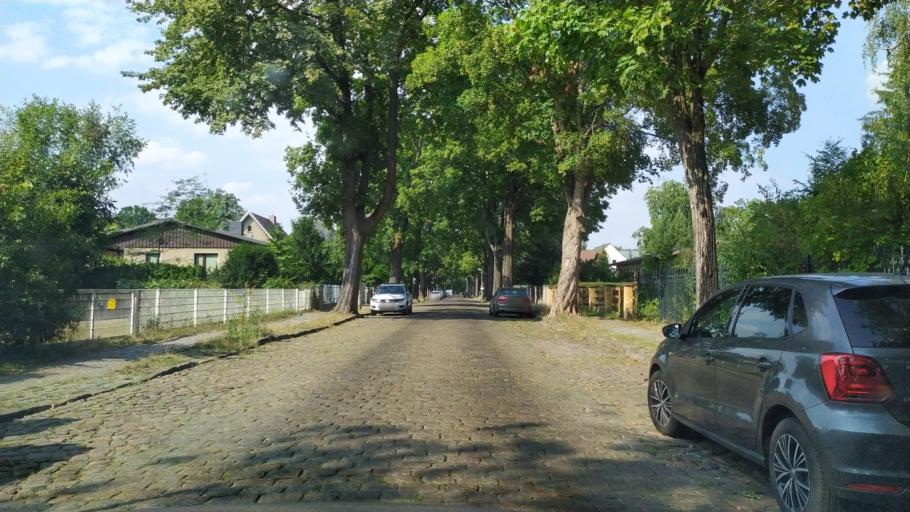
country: DE
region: Berlin
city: Grunau
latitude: 52.4199
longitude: 13.5919
